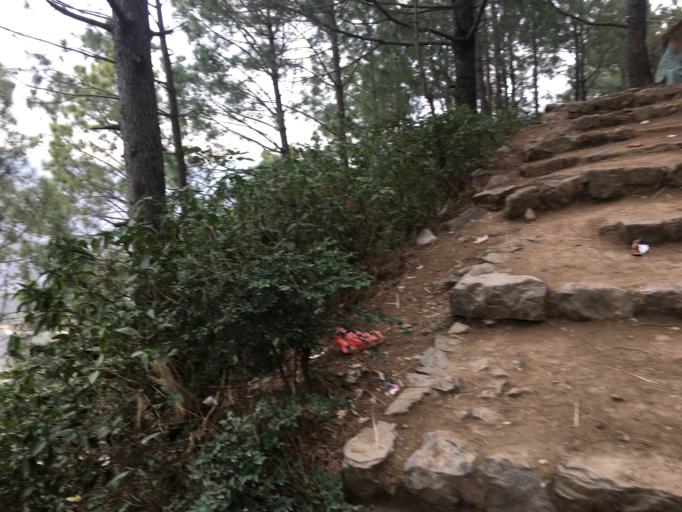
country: PK
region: Islamabad
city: Islamabad
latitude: 33.7608
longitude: 73.0675
